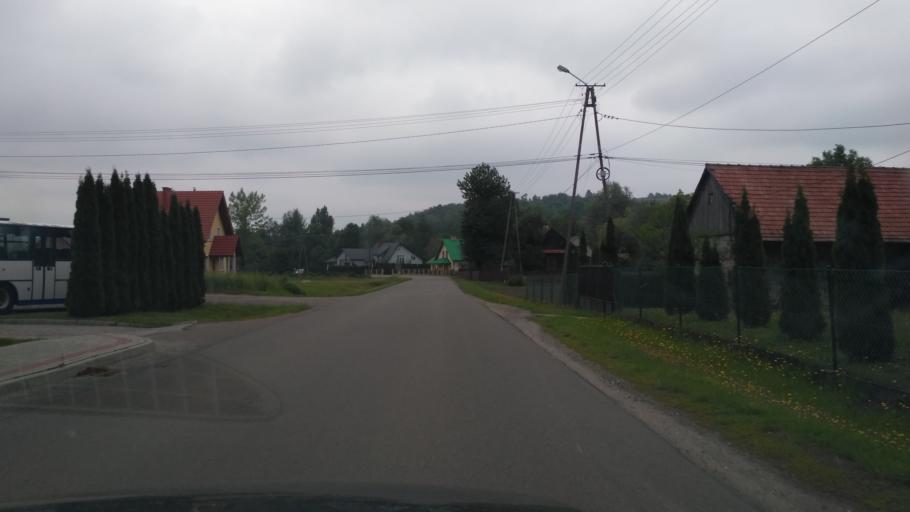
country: PL
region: Subcarpathian Voivodeship
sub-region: Powiat ropczycko-sedziszowski
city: Zagorzyce
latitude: 50.0190
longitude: 21.6776
